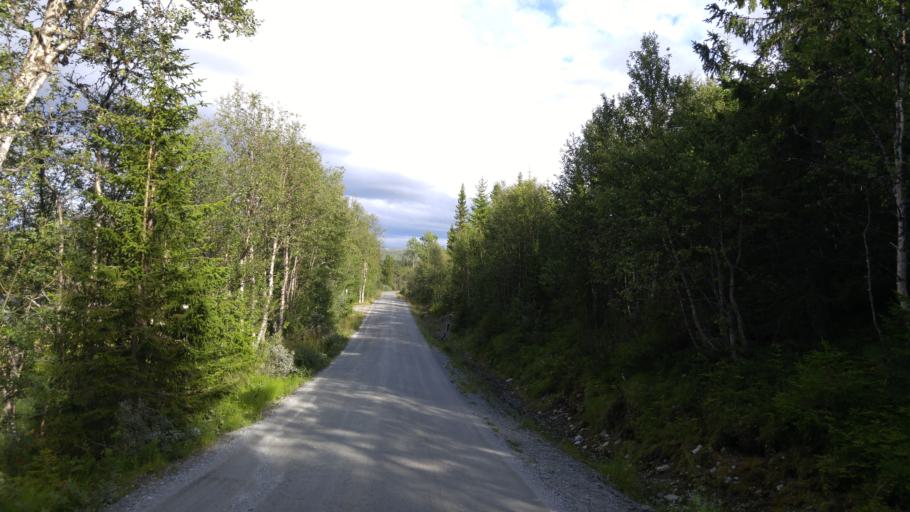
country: NO
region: Buskerud
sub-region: Hemsedal
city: Troim
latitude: 60.8476
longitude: 8.7188
